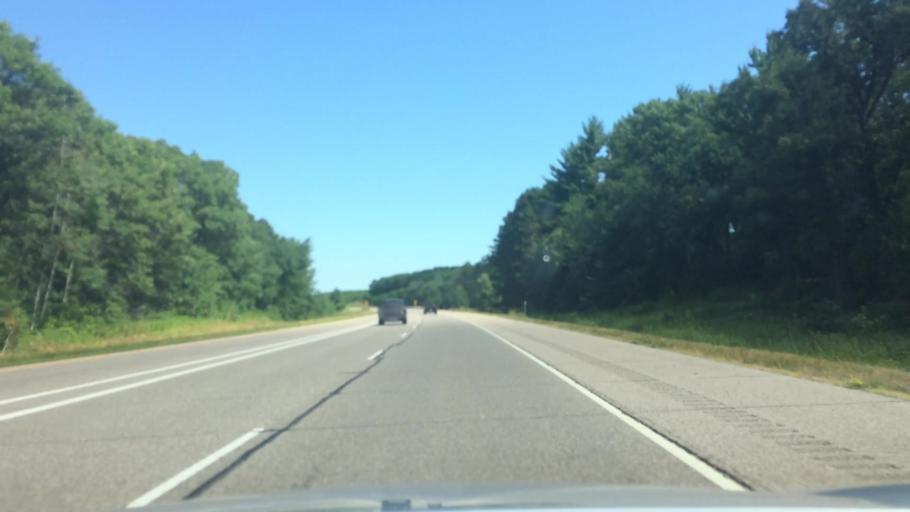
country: US
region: Wisconsin
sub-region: Marquette County
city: Westfield
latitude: 44.0803
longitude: -89.5328
